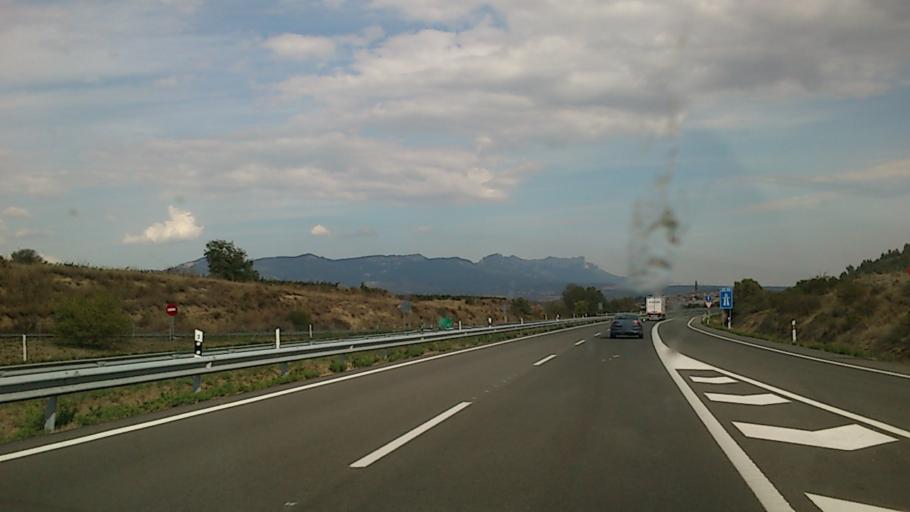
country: ES
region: La Rioja
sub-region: Provincia de La Rioja
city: Gimileo
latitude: 42.5388
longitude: -2.8164
